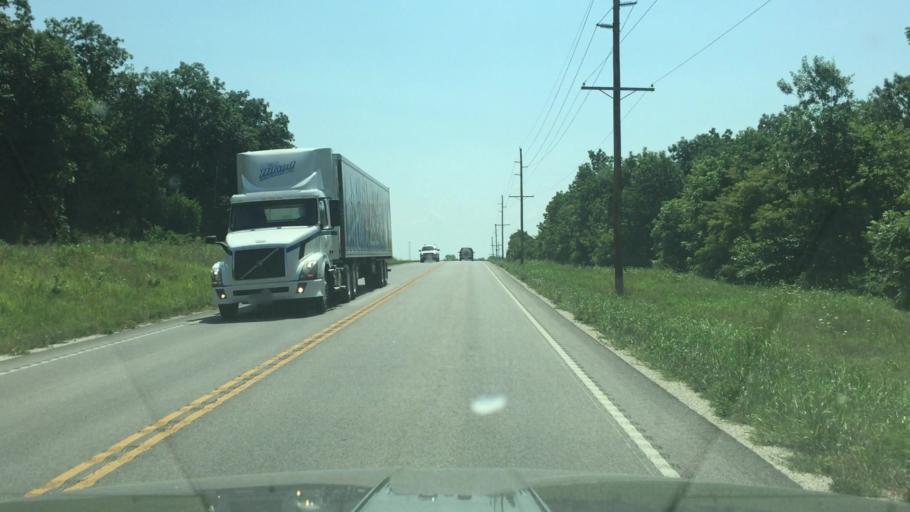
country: US
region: Missouri
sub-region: Miller County
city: Eldon
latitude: 38.3875
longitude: -92.6955
